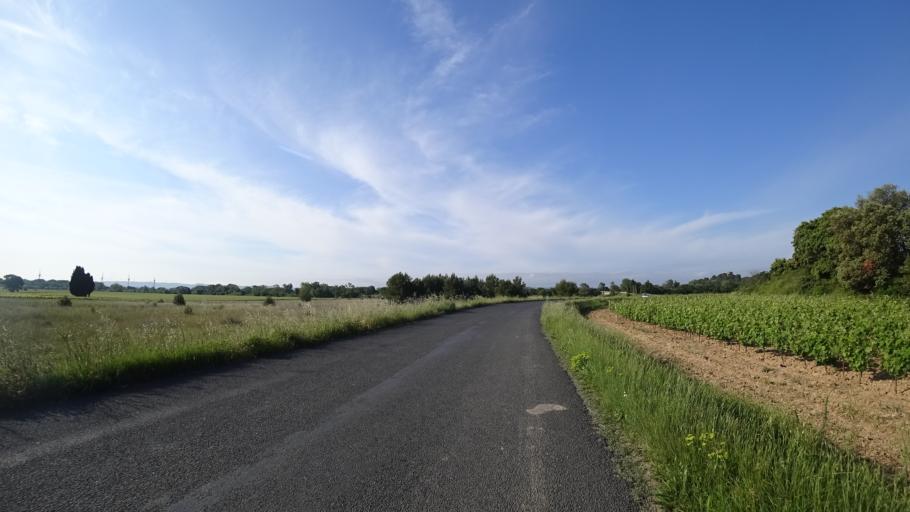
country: FR
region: Languedoc-Roussillon
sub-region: Departement de l'Aude
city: Canet
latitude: 43.2418
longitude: 2.7996
